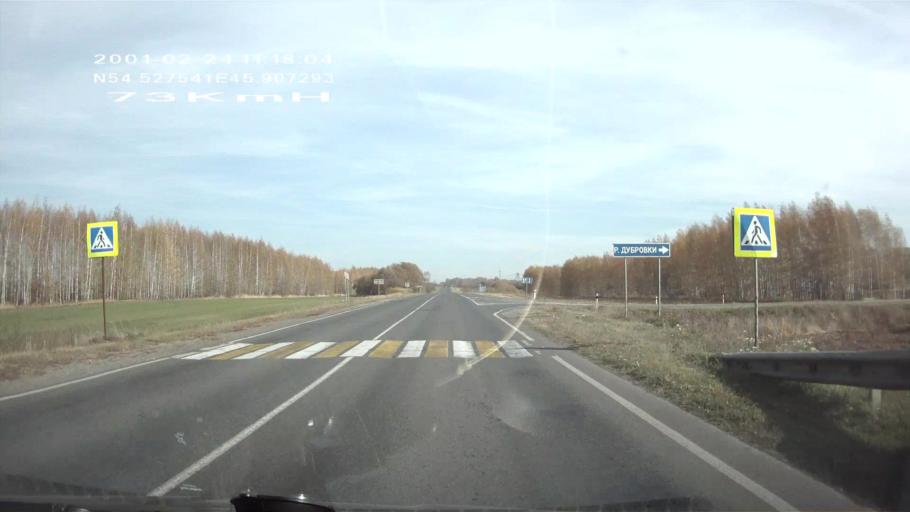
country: RU
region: Mordoviya
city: Atyashevo
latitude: 54.5273
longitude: 45.9070
